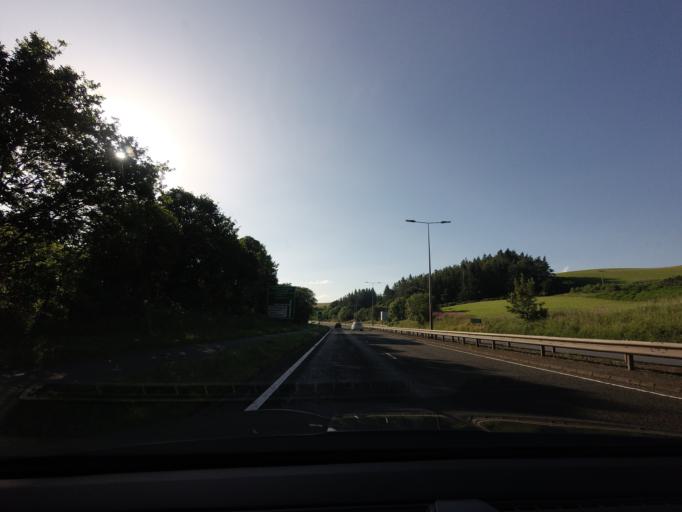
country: GB
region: Scotland
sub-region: Highland
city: Inverness
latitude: 57.5064
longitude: -4.2568
